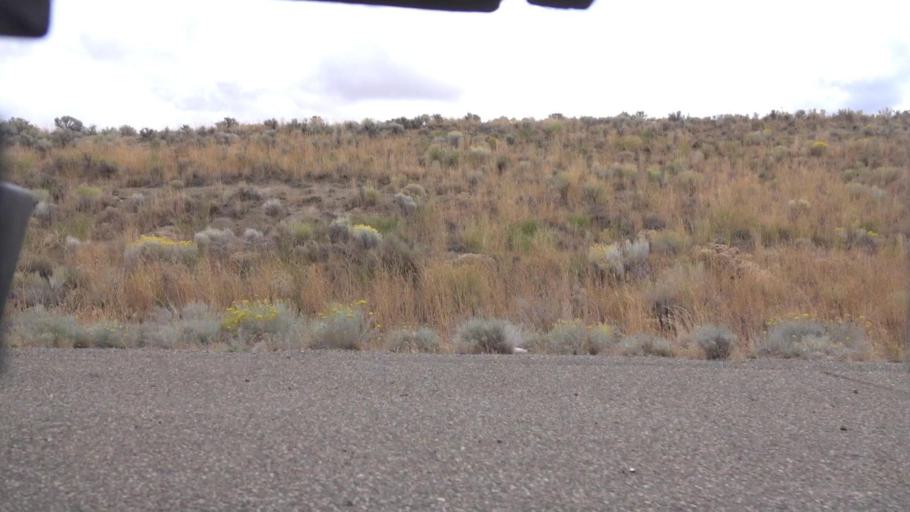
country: US
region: Nevada
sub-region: Elko County
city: Elko
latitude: 40.8960
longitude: -115.7090
